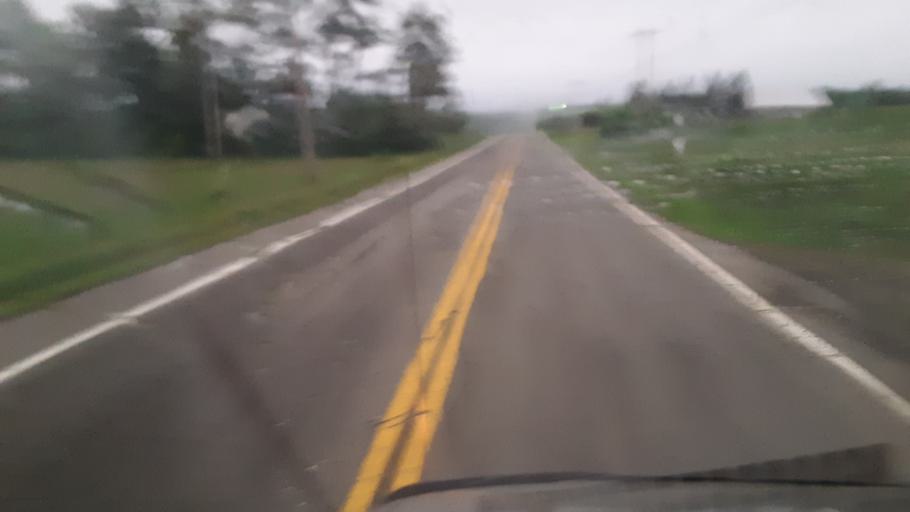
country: US
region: Maine
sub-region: Penobscot County
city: Patten
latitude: 46.0437
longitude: -68.4438
